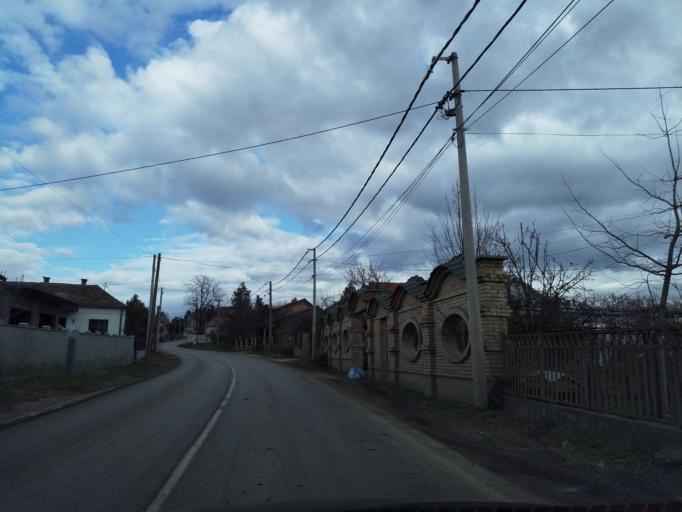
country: RS
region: Central Serbia
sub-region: Belgrade
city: Grocka
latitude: 44.6003
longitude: 20.7259
